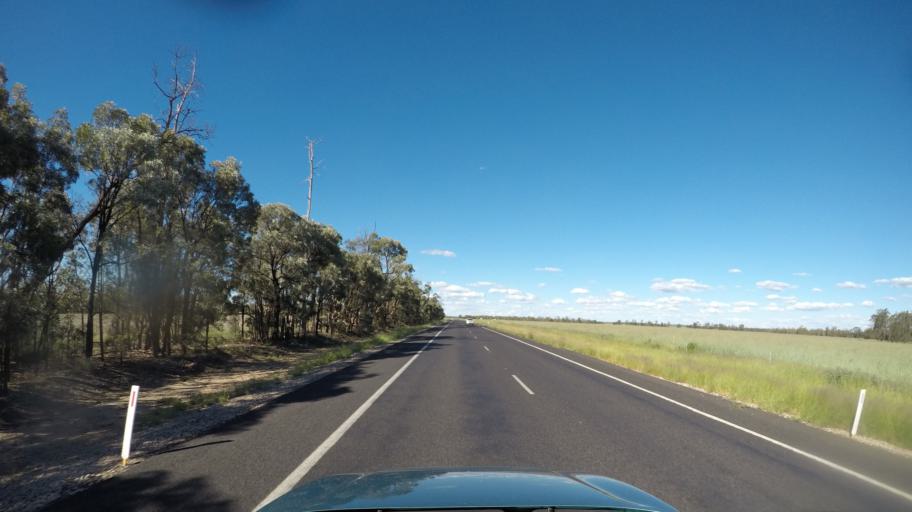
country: AU
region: Queensland
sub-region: Goondiwindi
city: Goondiwindi
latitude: -28.1302
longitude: 150.7004
